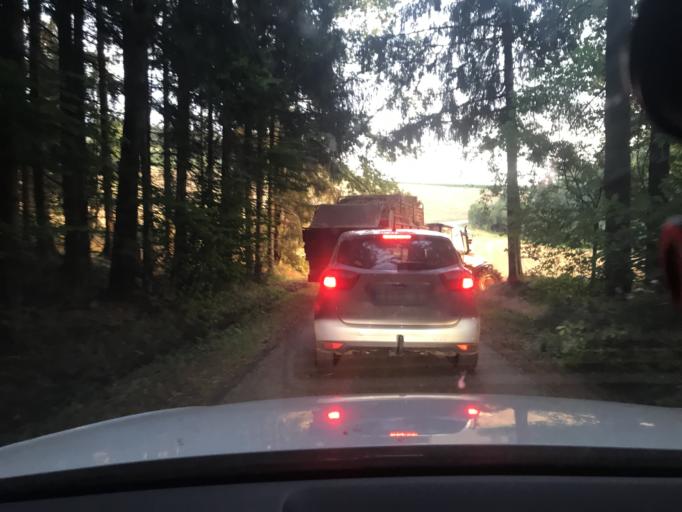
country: DE
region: Bavaria
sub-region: Upper Palatinate
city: Auerbach
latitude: 49.7423
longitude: 11.6169
